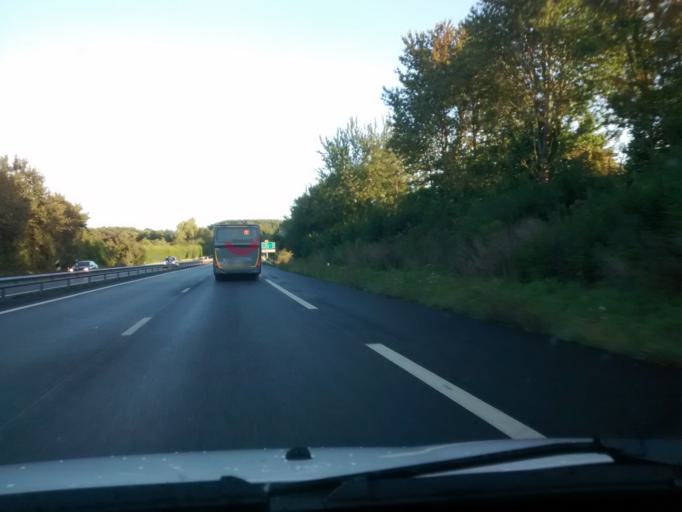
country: FR
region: Brittany
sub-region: Departement d'Ille-et-Vilaine
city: Tinteniac
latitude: 48.3302
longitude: -1.8562
